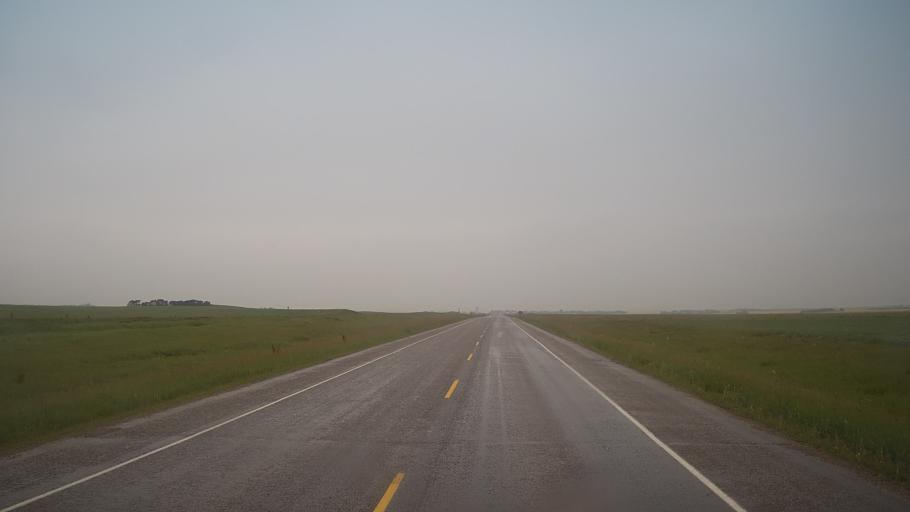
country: CA
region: Saskatchewan
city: Wilkie
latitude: 52.1862
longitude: -108.3993
